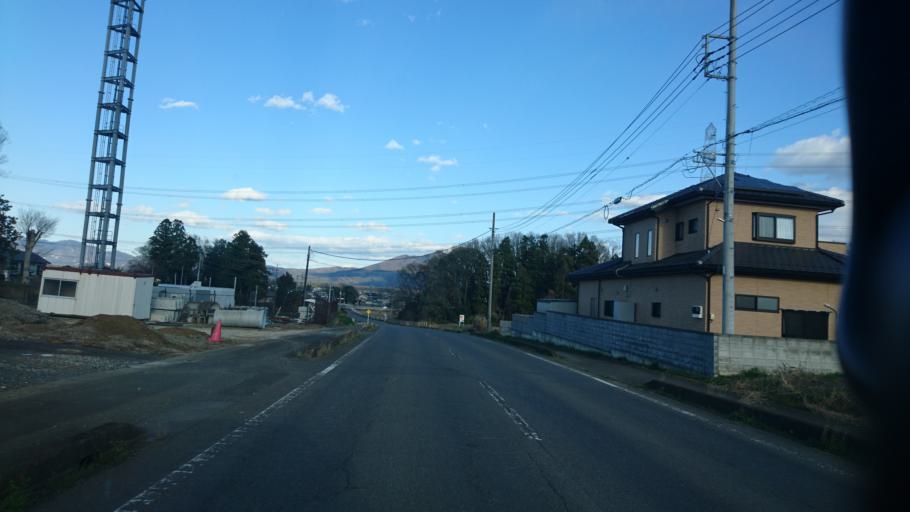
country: JP
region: Ibaraki
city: Shimodate
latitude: 36.2397
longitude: 139.9796
